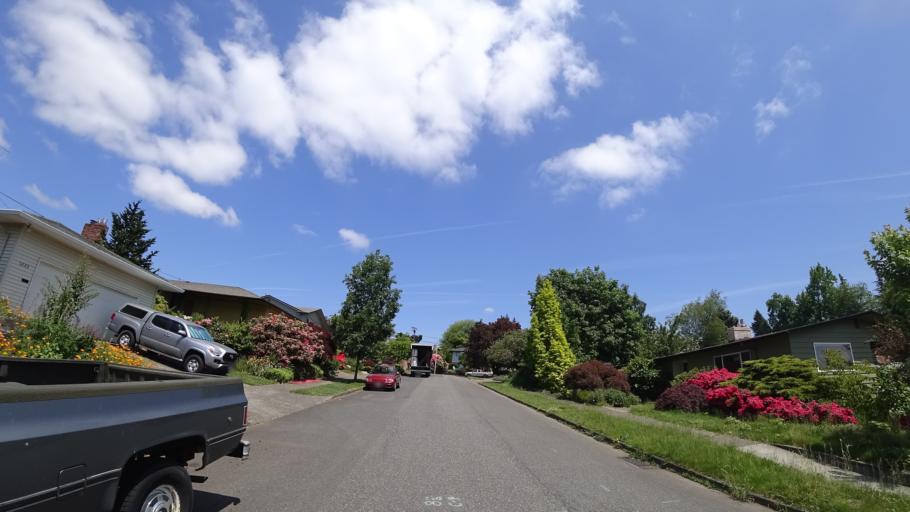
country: US
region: Oregon
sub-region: Multnomah County
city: Portland
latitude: 45.4729
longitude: -122.6911
